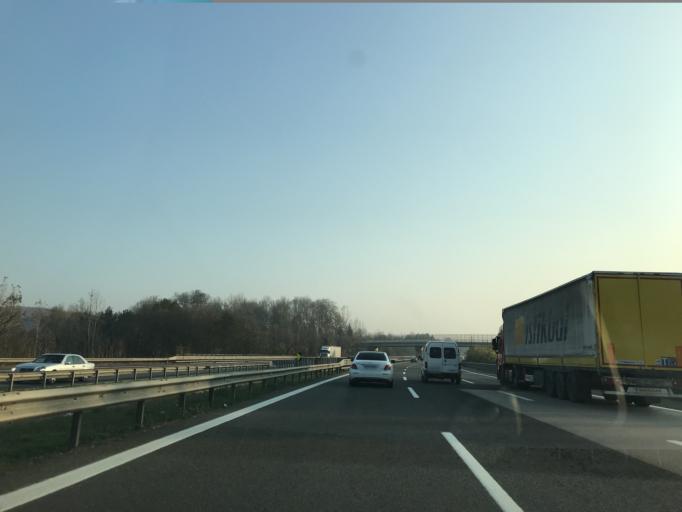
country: TR
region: Sakarya
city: Hendek
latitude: 40.7782
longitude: 30.7903
